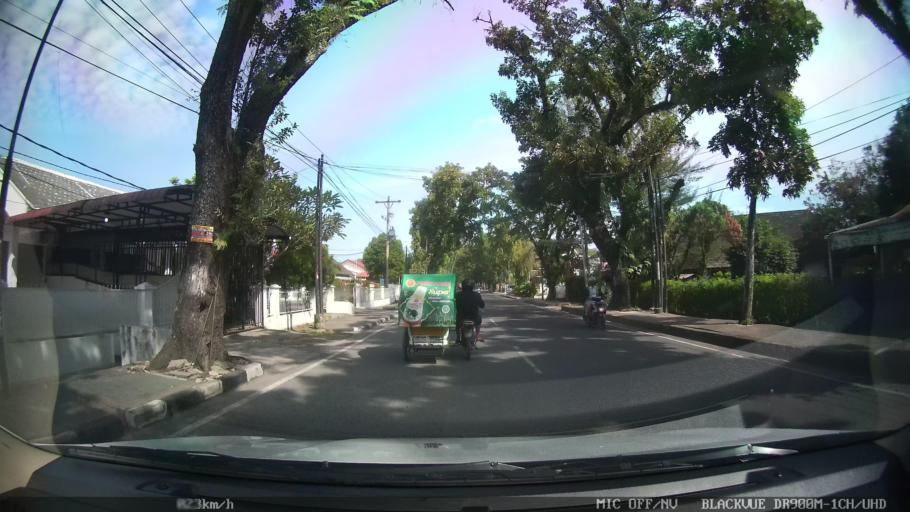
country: ID
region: North Sumatra
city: Medan
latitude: 3.5721
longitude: 98.6600
